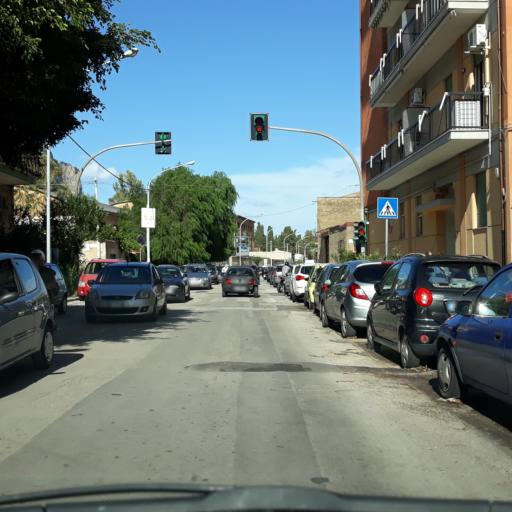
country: IT
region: Sicily
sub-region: Palermo
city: Palermo
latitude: 38.1545
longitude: 13.3706
